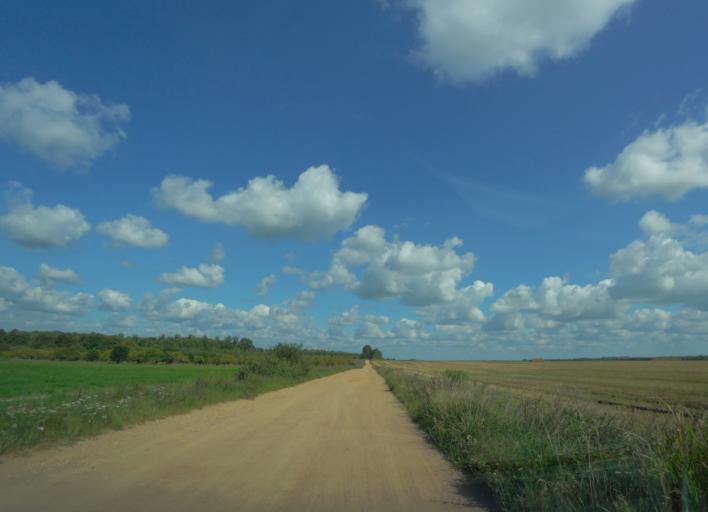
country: BY
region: Minsk
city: Zyembin
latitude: 54.3756
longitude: 28.3452
